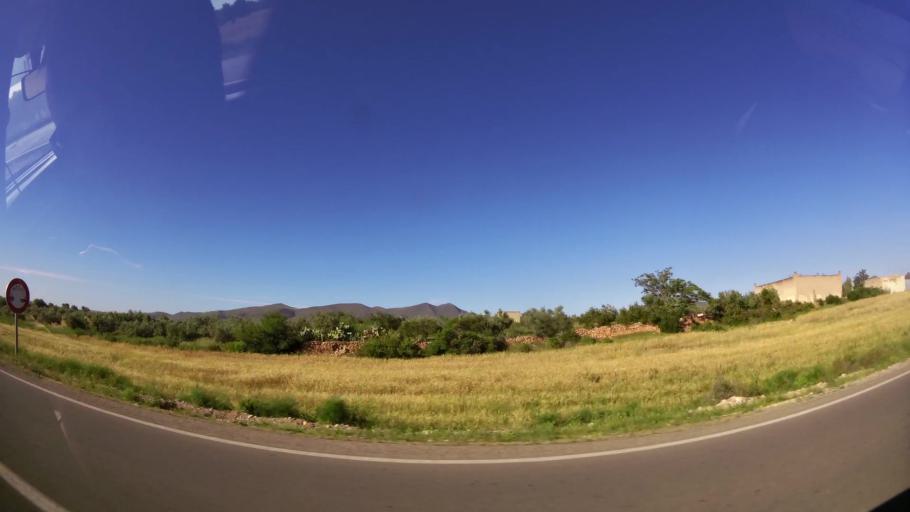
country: MA
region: Oriental
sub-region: Berkane-Taourirt
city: Ahfir
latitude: 34.9689
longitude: -2.1202
